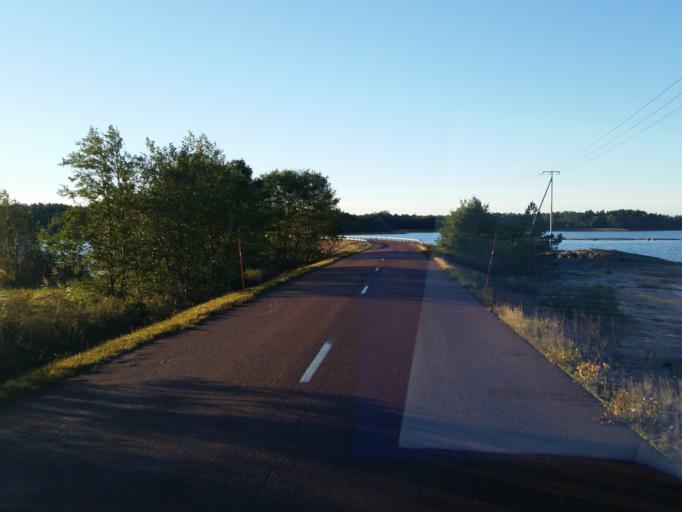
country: AX
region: Alands skaergard
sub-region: Vardoe
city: Vardoe
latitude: 60.3130
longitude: 20.3743
